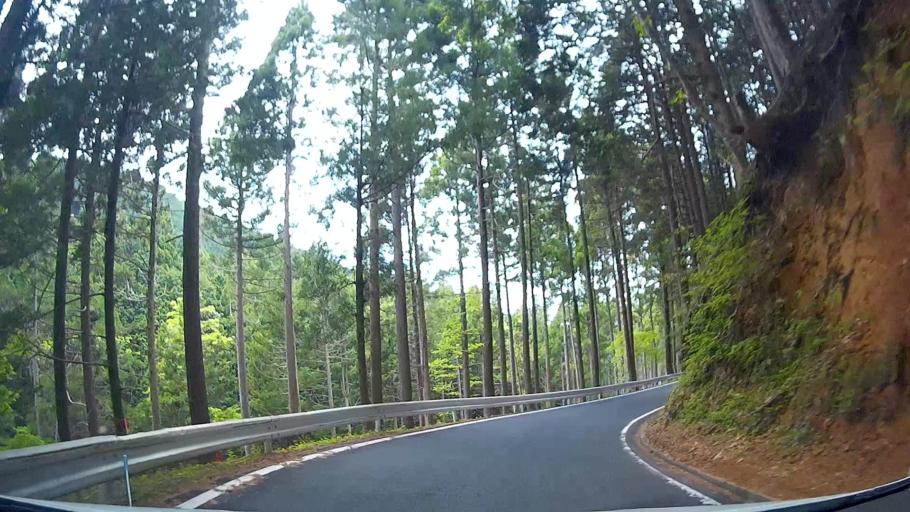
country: JP
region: Shizuoka
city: Ito
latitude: 34.9072
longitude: 139.0522
